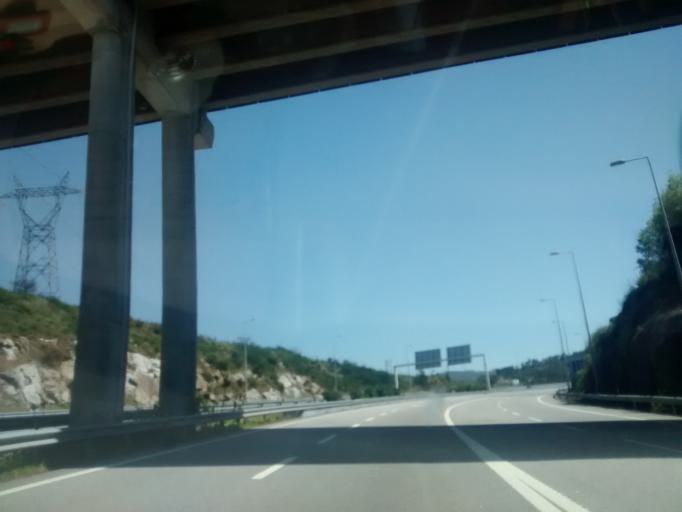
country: PT
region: Braga
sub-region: Guimaraes
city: Candoso
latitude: 41.4289
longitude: -8.3344
